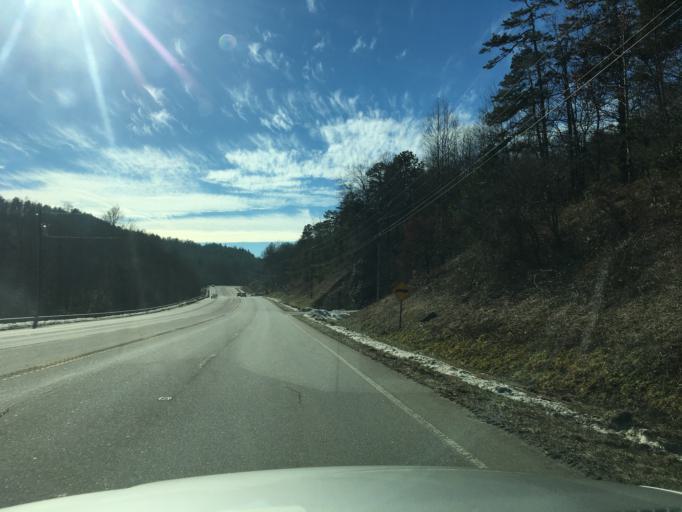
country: US
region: North Carolina
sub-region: Henderson County
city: Etowah
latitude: 35.3054
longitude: -82.6701
